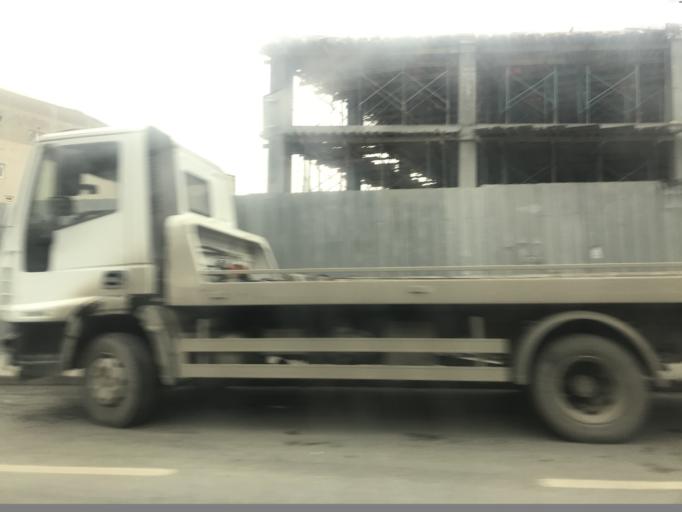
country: TR
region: Istanbul
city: Mahmutbey
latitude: 41.0451
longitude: 28.8182
